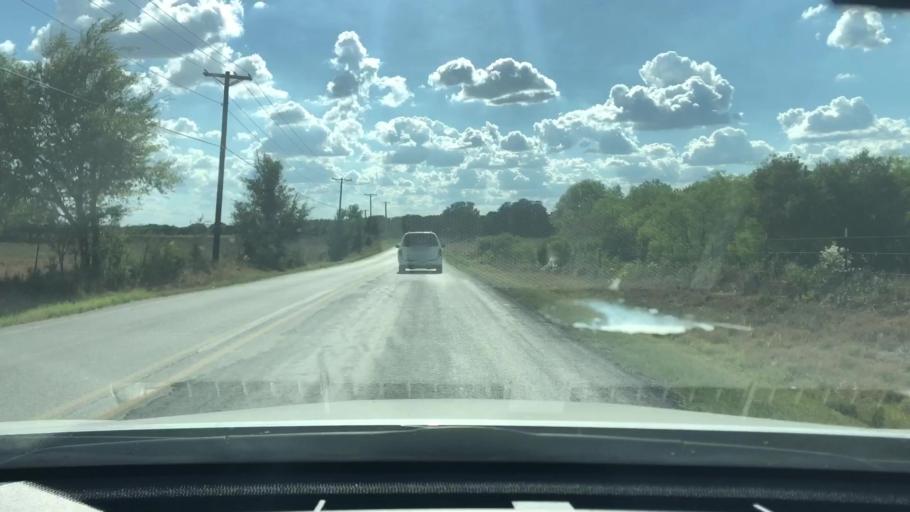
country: US
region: Texas
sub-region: Guadalupe County
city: Northcliff
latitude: 29.6564
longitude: -98.2066
